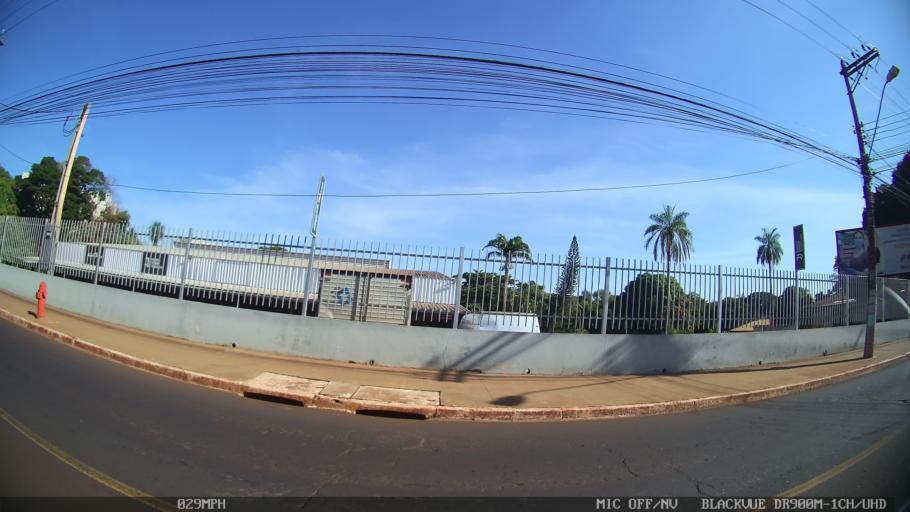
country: BR
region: Sao Paulo
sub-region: Ribeirao Preto
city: Ribeirao Preto
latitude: -21.1834
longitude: -47.7724
